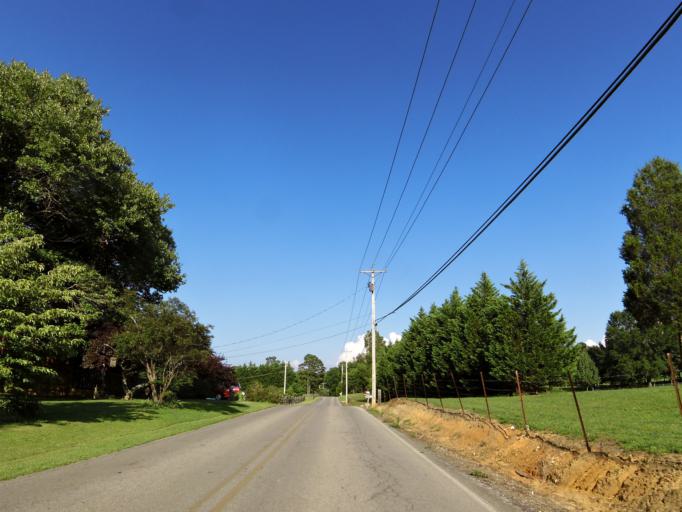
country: US
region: Tennessee
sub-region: Blount County
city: Maryville
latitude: 35.7231
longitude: -83.9346
